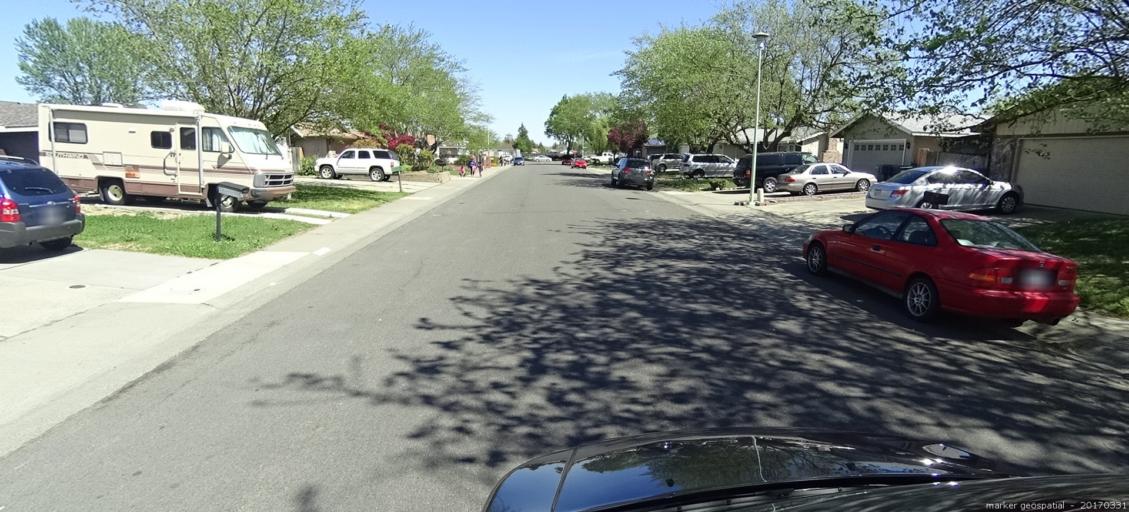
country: US
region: California
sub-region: Sacramento County
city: Laguna
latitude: 38.4528
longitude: -121.4401
